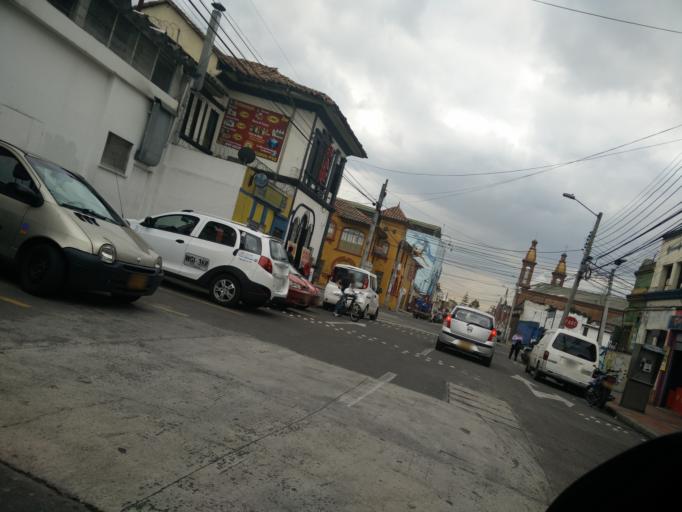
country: CO
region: Bogota D.C.
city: Bogota
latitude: 4.6512
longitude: -74.0670
